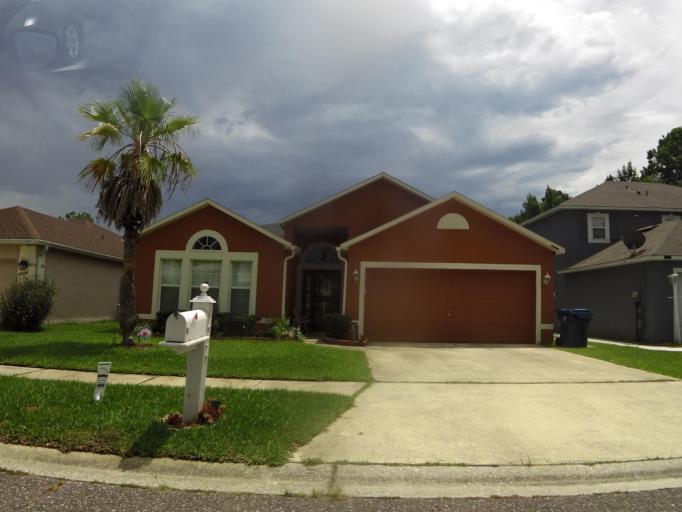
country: US
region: Florida
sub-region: Nassau County
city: Nassau Village-Ratliff
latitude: 30.4243
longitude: -81.7303
